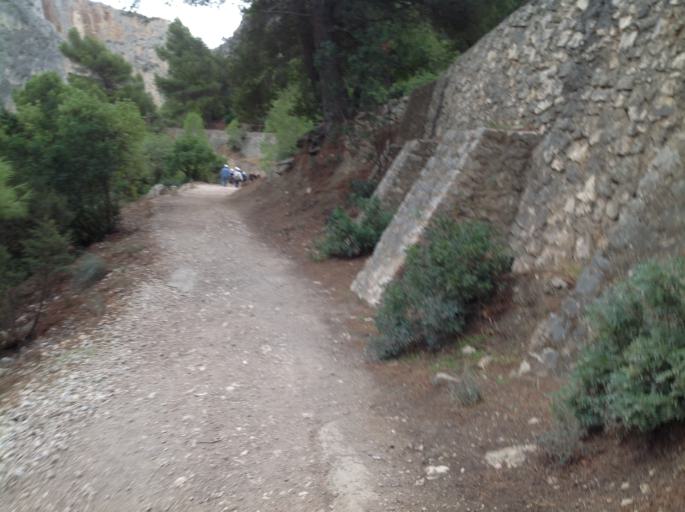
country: ES
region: Andalusia
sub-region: Provincia de Malaga
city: Carratraca
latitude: 36.9199
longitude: -4.7790
